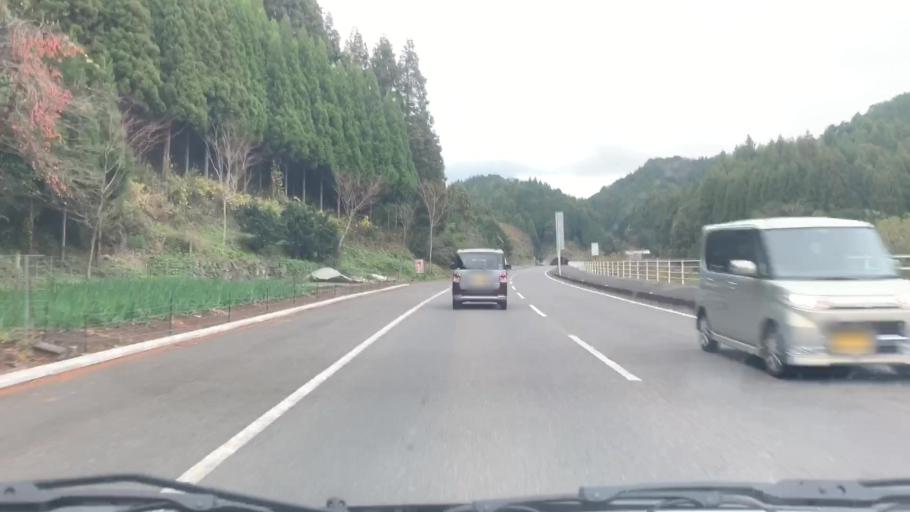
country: JP
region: Saga Prefecture
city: Ureshinomachi-shimojuku
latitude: 33.0946
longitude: 130.0297
